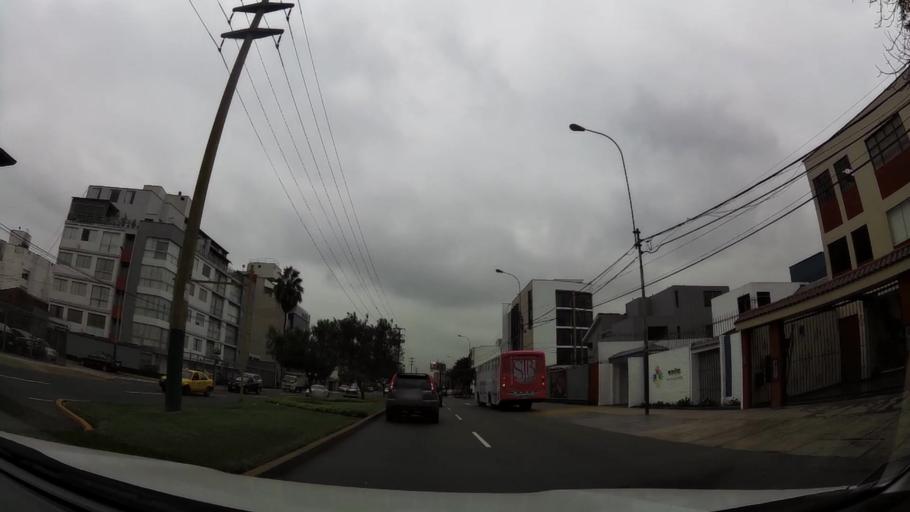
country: PE
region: Lima
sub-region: Lima
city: Surco
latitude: -12.1183
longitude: -76.9891
